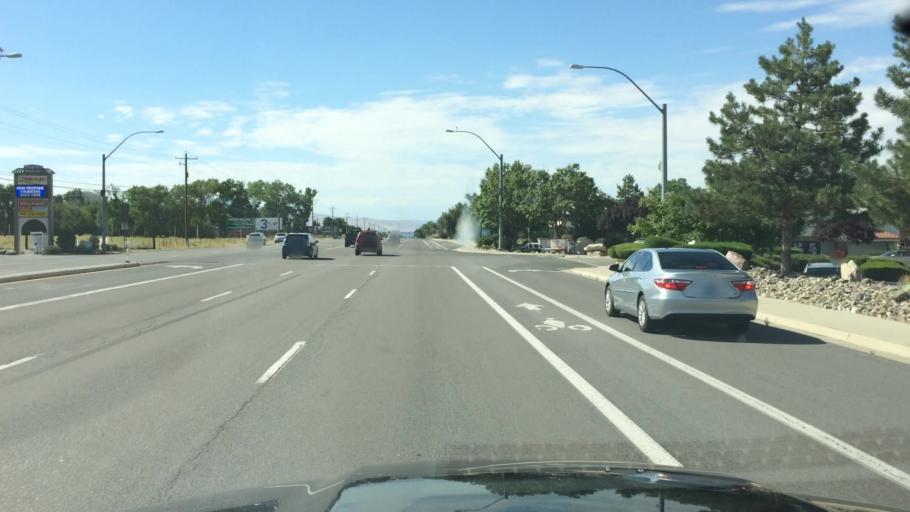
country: US
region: Nevada
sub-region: Washoe County
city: Sparks
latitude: 39.4211
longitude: -119.7579
